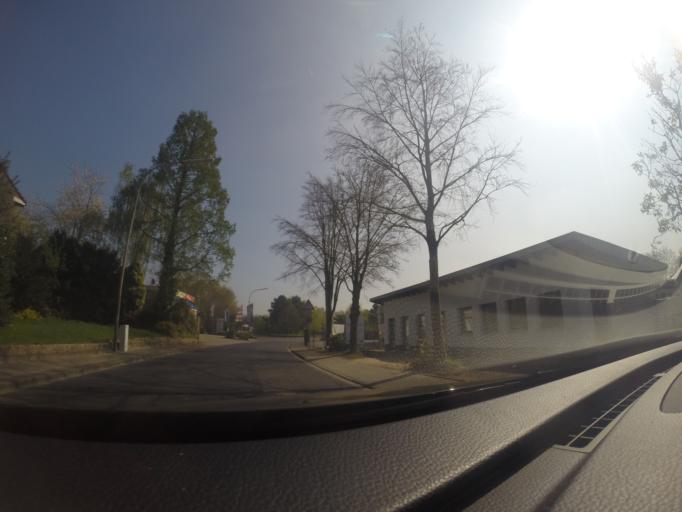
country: DE
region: North Rhine-Westphalia
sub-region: Regierungsbezirk Dusseldorf
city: Xanten
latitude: 51.6582
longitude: 6.4443
